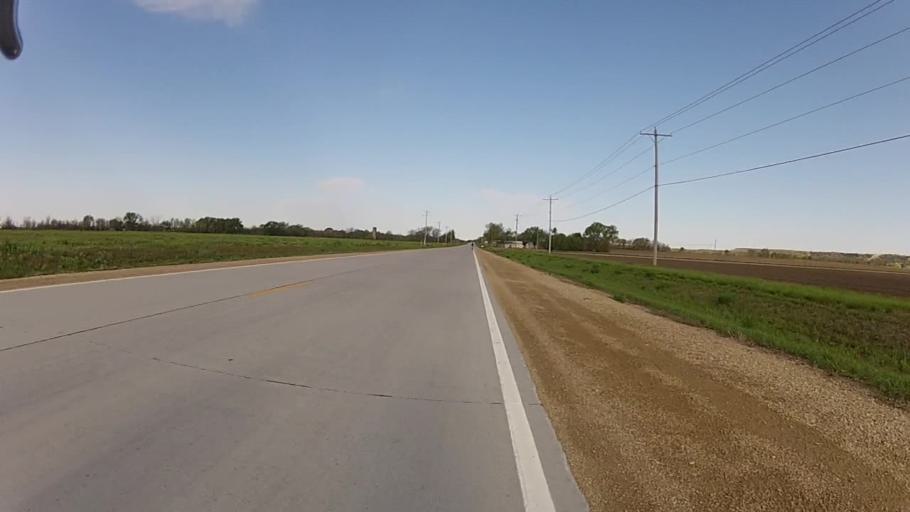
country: US
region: Kansas
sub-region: Riley County
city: Ogden
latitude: 39.1532
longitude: -96.6661
